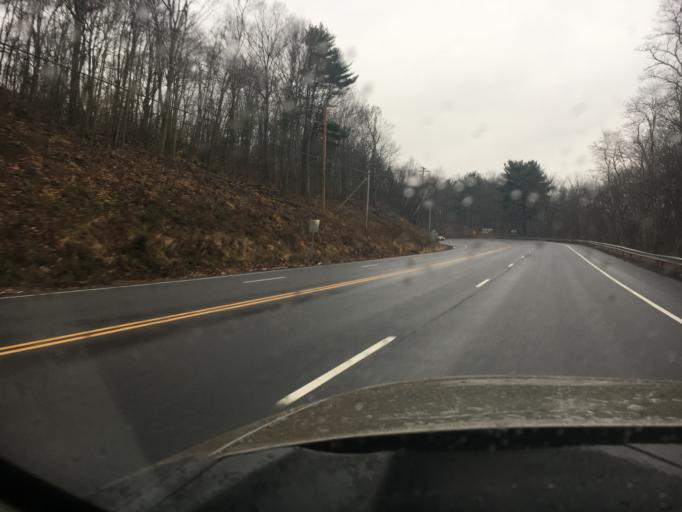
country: US
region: Pennsylvania
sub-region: Luzerne County
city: Harleigh
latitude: 41.0287
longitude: -75.9613
